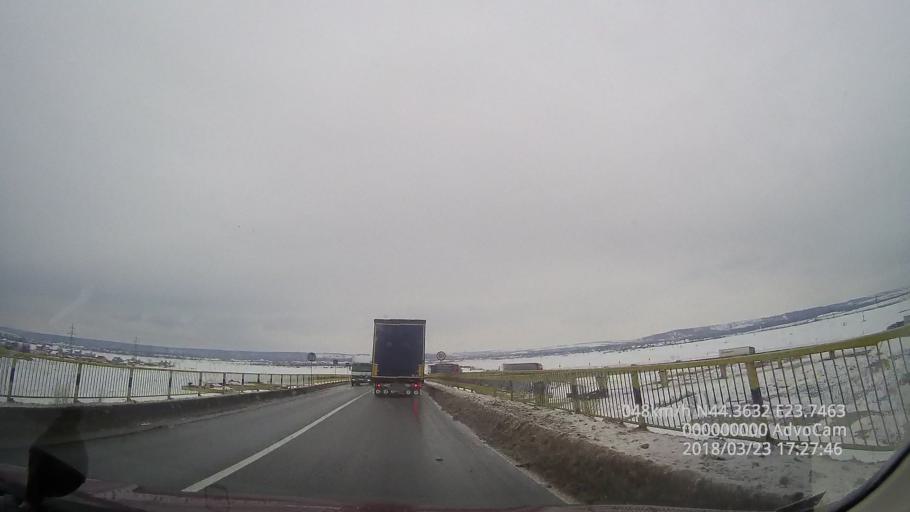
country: RO
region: Dolj
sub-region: Municipiul Craiova
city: Cernele
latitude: 44.3628
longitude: 23.7455
